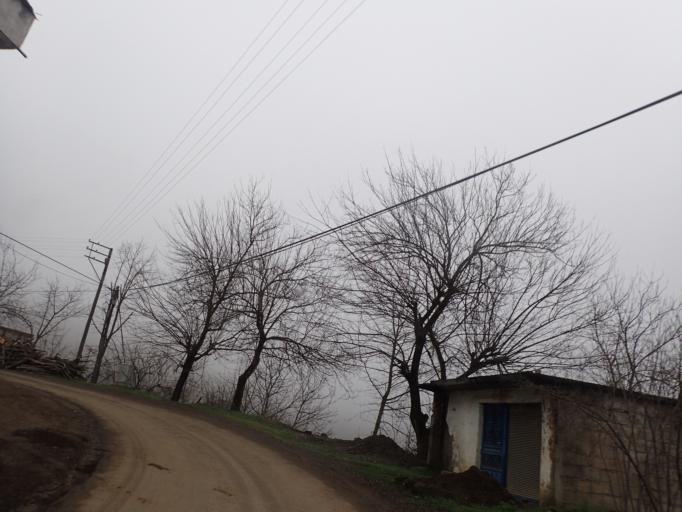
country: TR
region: Ordu
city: Camas
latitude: 40.9212
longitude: 37.5572
